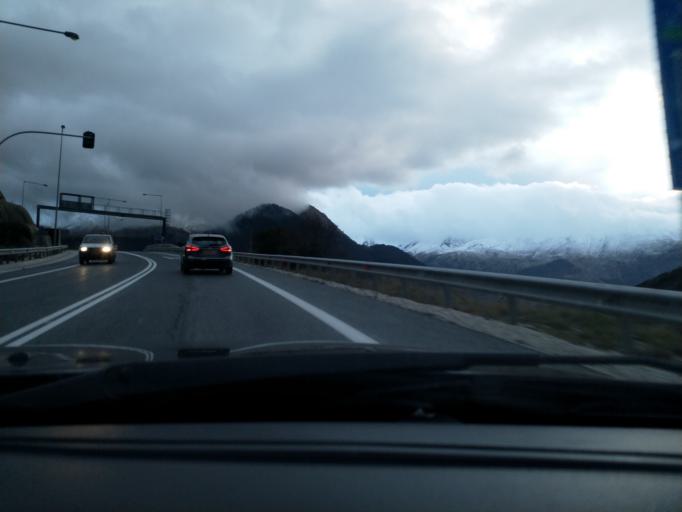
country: GR
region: Epirus
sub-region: Nomos Ioanninon
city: Metsovo
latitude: 39.7626
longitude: 21.1716
